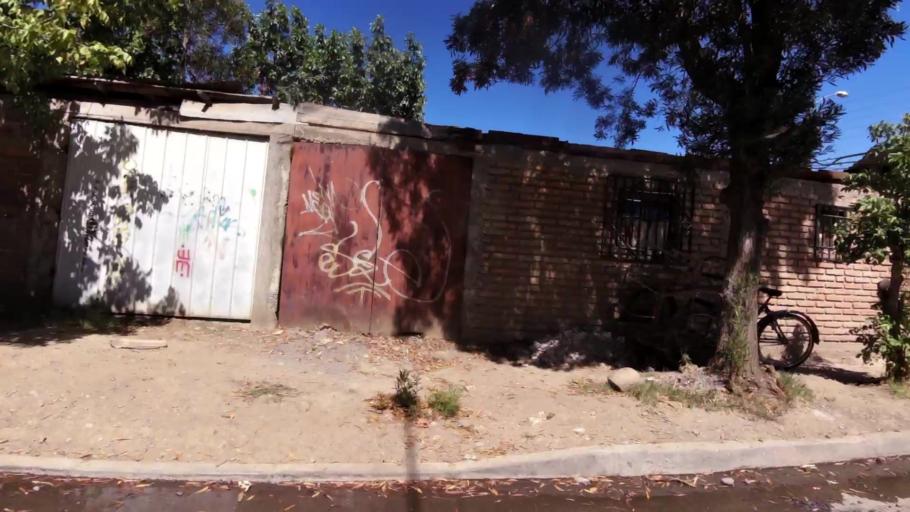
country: CL
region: O'Higgins
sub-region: Provincia de Colchagua
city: Chimbarongo
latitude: -34.5707
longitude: -70.9965
